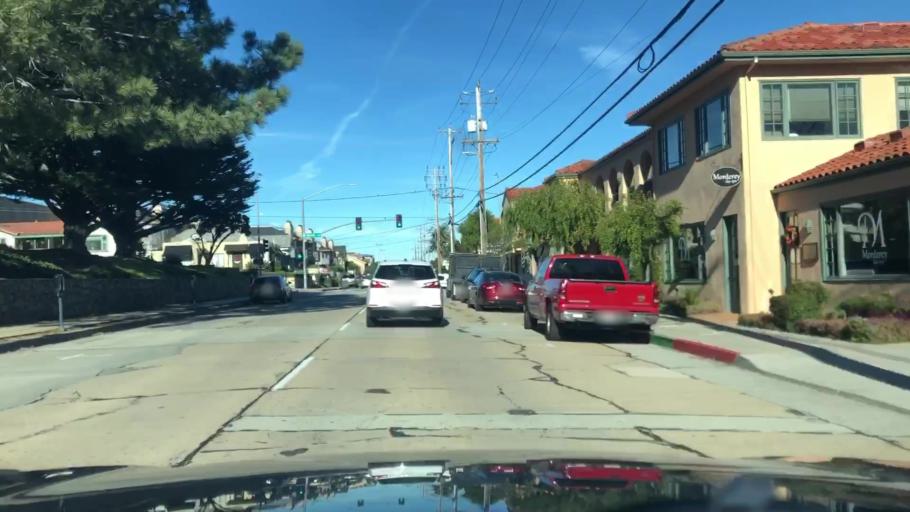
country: US
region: California
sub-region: Monterey County
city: Monterey
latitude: 36.6115
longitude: -121.8987
